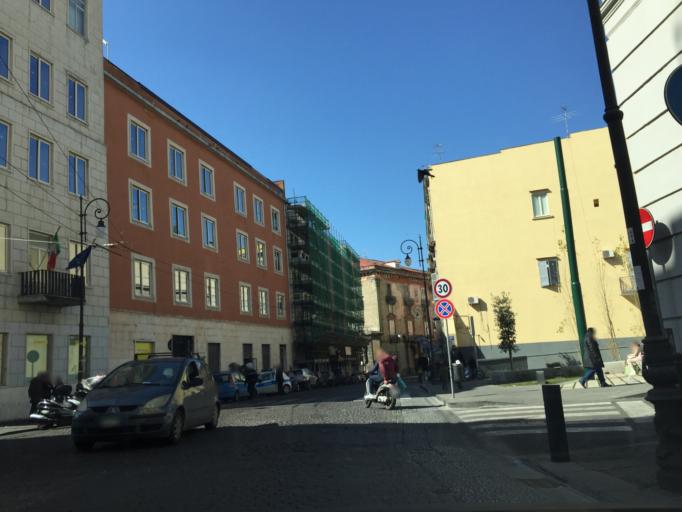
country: IT
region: Campania
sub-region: Provincia di Napoli
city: Portici
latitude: 40.8143
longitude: 14.3370
